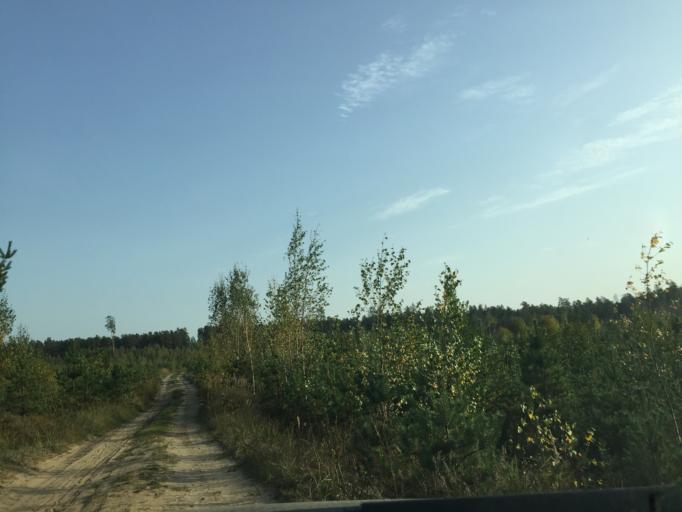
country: LV
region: Garkalne
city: Garkalne
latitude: 56.9696
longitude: 24.4187
